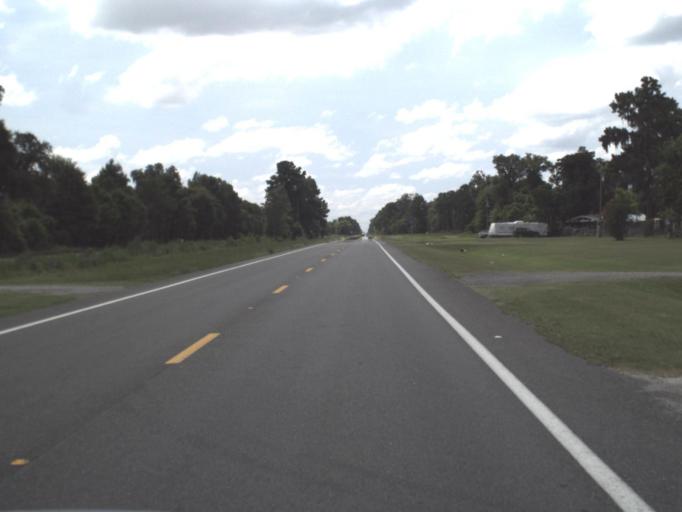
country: US
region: Florida
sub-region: Hamilton County
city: Jasper
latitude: 30.4735
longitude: -82.9100
